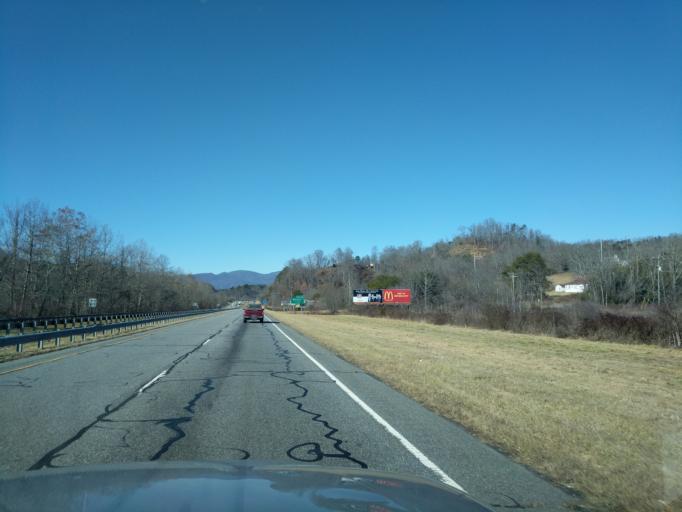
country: US
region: North Carolina
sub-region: Swain County
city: Cherokee
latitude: 35.4234
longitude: -83.3477
